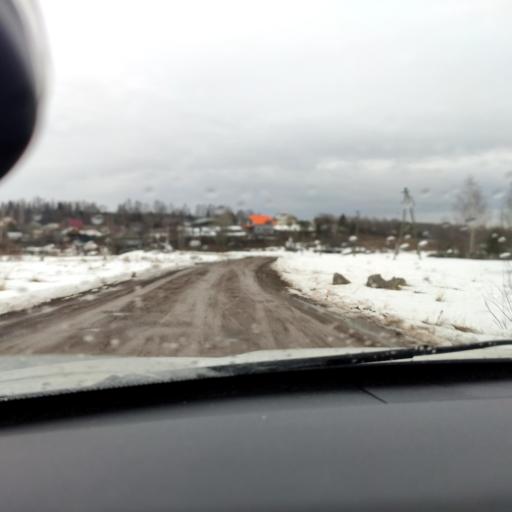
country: RU
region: Perm
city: Lobanovo
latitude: 57.8524
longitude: 56.3419
